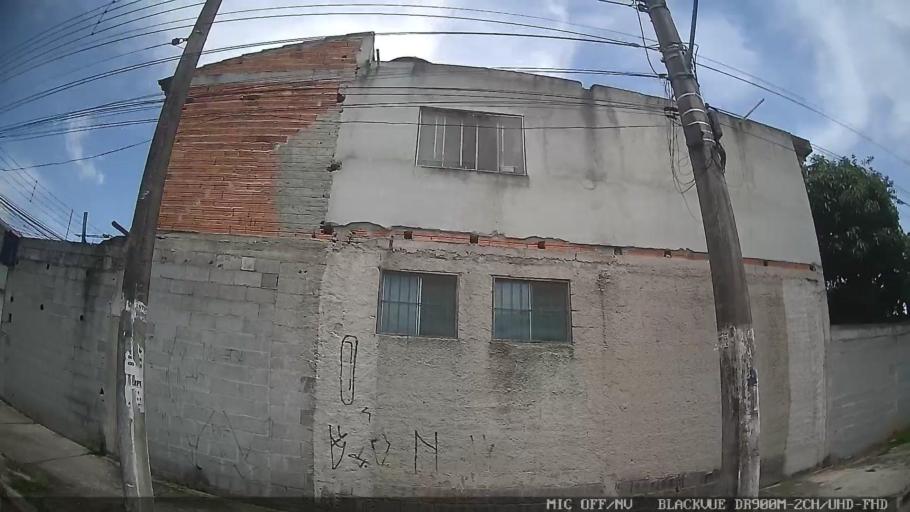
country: BR
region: Sao Paulo
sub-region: Suzano
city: Suzano
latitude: -23.5256
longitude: -46.3075
